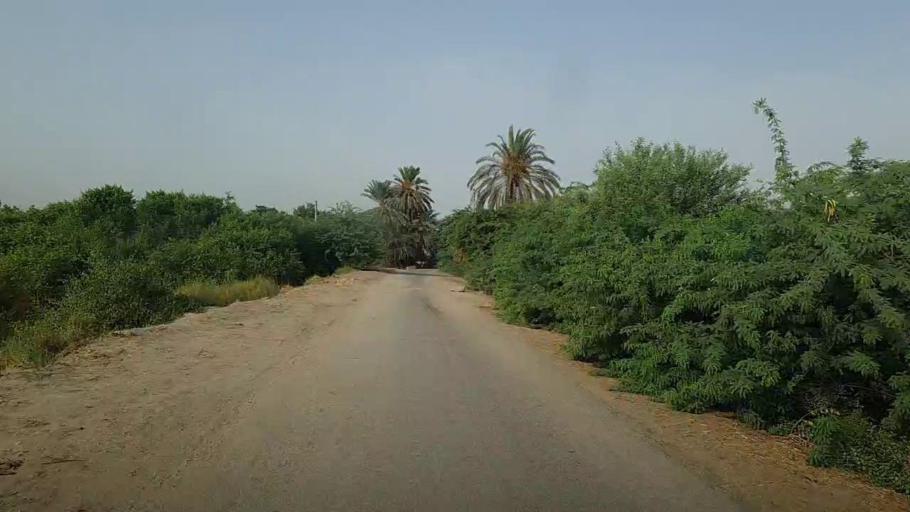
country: PK
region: Sindh
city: Mehar
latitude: 27.1487
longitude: 67.7991
